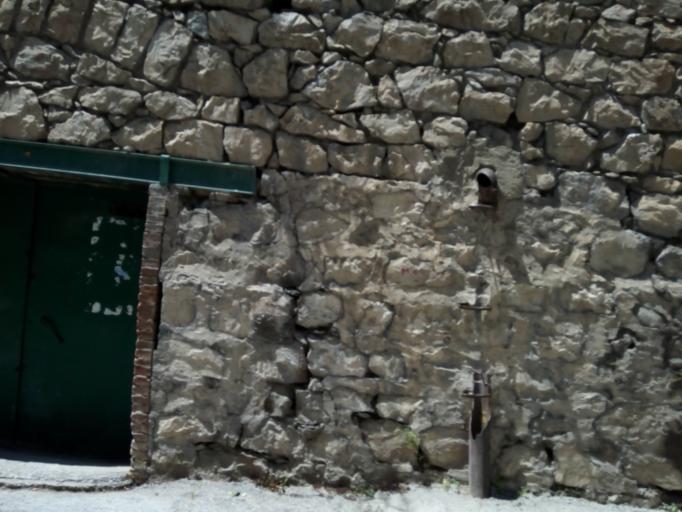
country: DZ
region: Constantine
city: Constantine
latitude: 36.3705
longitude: 6.6196
